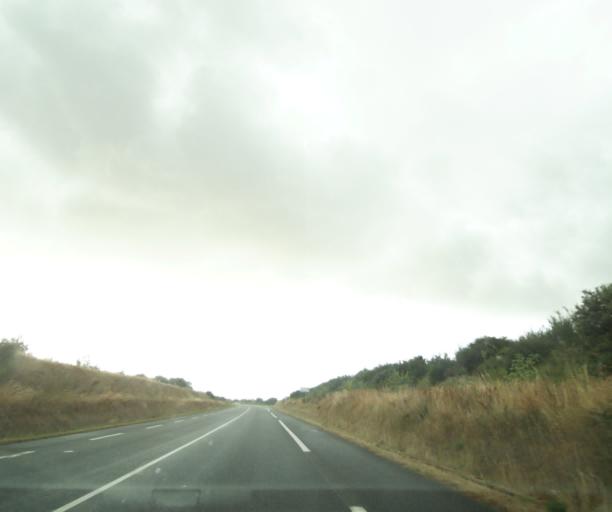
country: FR
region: Pays de la Loire
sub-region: Departement de la Vendee
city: Saint-Hilaire-de-Talmont
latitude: 46.4654
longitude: -1.6425
